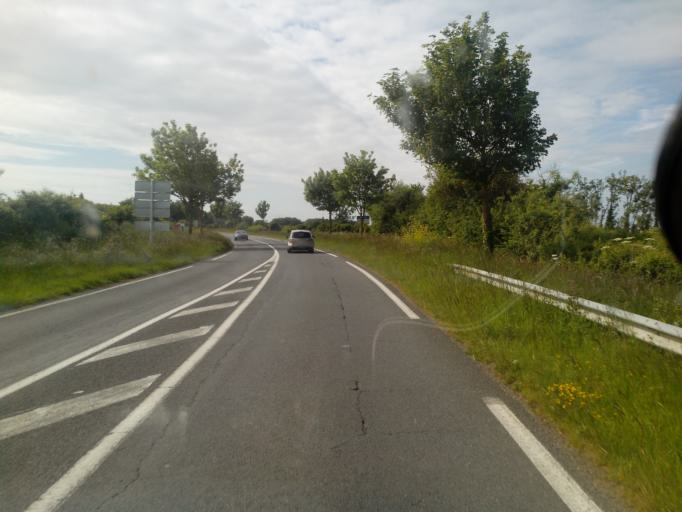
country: FR
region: Lower Normandy
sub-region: Departement du Calvados
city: Dives-sur-Mer
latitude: 49.2729
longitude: -0.1046
